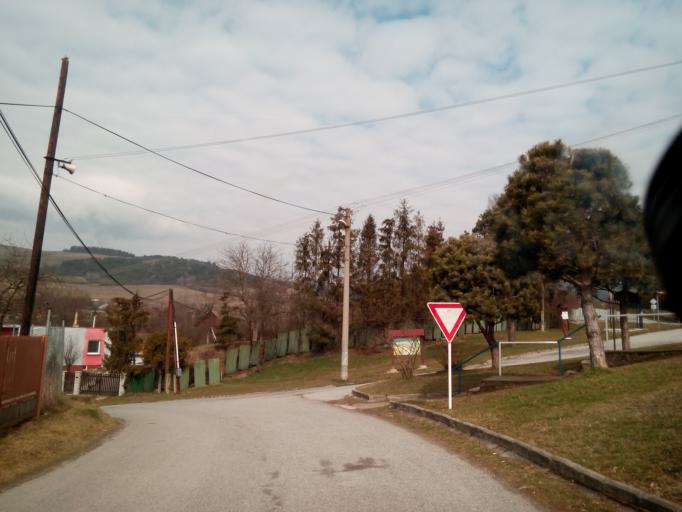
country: SK
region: Presovsky
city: Sabinov
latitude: 49.0461
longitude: 21.0197
